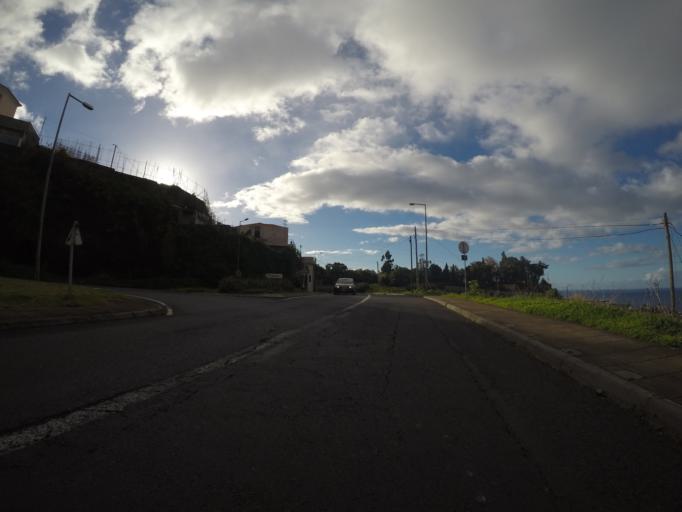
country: PT
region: Madeira
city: Camara de Lobos
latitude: 32.6483
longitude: -16.9581
